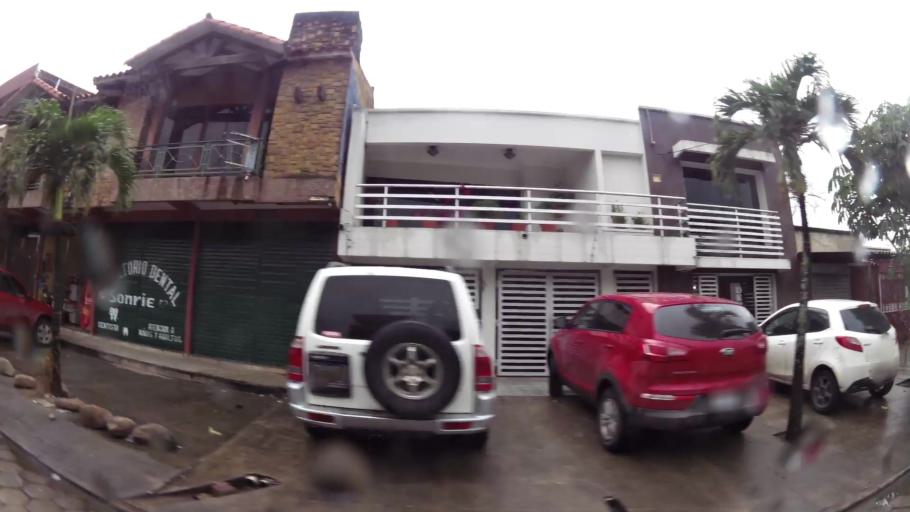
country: BO
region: Santa Cruz
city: Santa Cruz de la Sierra
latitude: -17.8071
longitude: -63.1982
